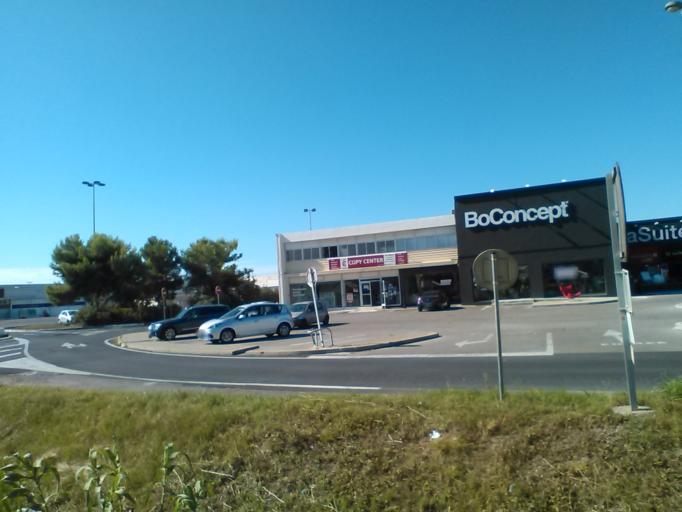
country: FR
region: Languedoc-Roussillon
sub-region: Departement de l'Herault
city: Perols
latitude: 43.5747
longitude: 3.9416
